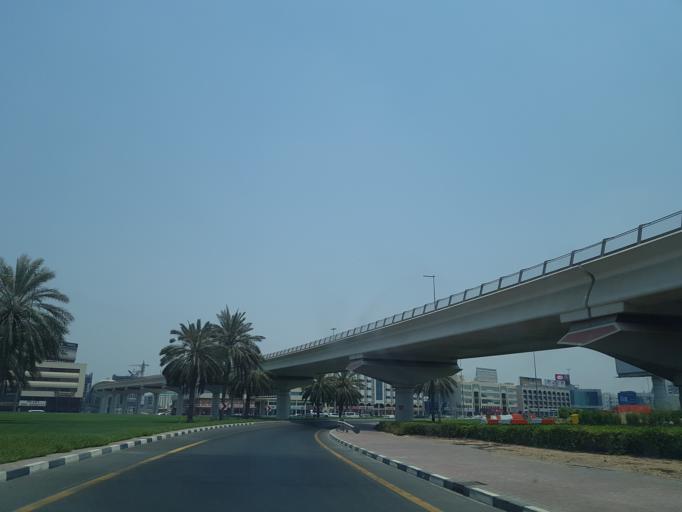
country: AE
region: Ash Shariqah
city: Sharjah
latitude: 25.2492
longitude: 55.3353
